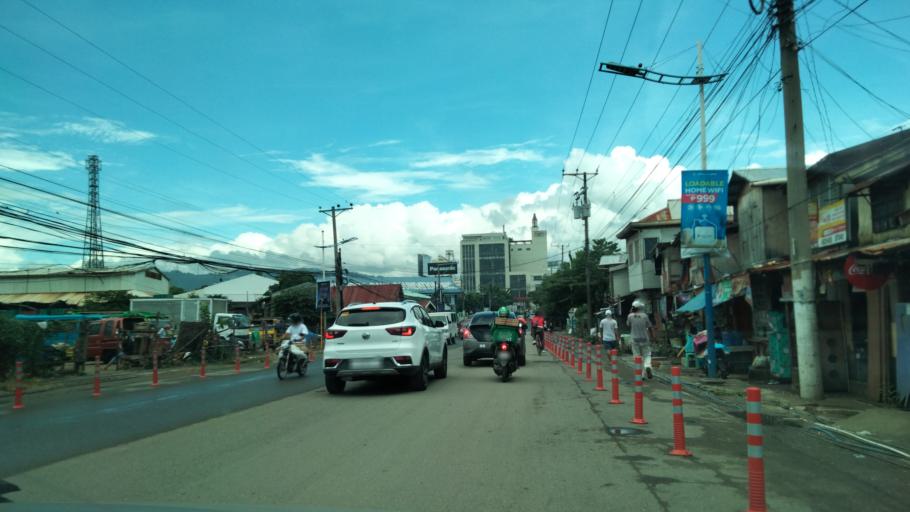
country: PH
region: Central Visayas
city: Mandaue City
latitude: 10.3277
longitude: 123.9340
